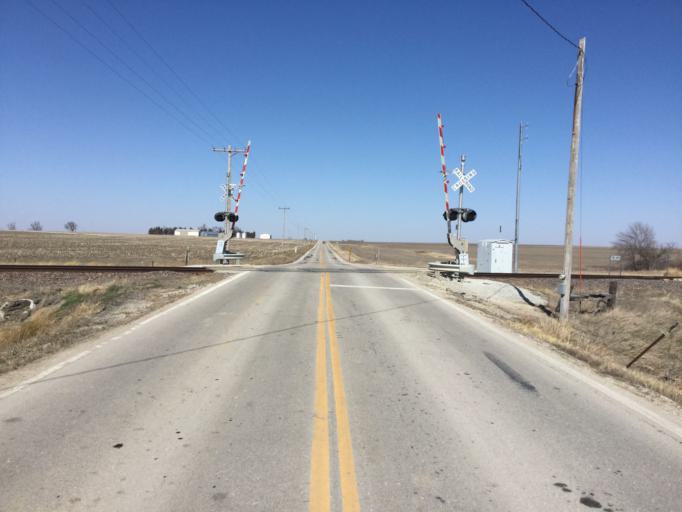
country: US
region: Nebraska
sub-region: Pawnee County
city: Pawnee City
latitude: 39.8961
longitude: -96.3513
